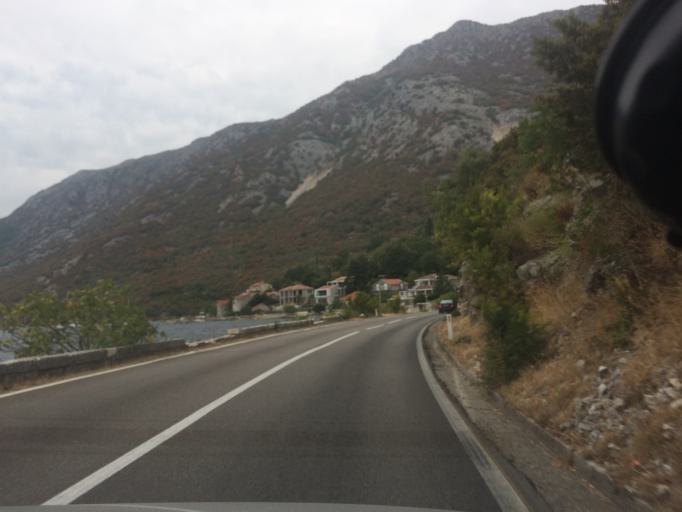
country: ME
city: Lipci
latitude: 42.5048
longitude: 18.6748
